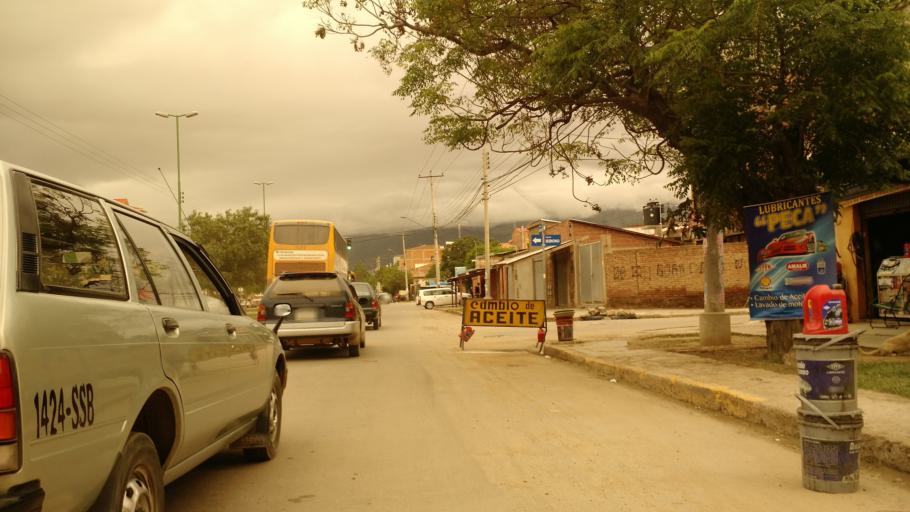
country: BO
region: Cochabamba
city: Cochabamba
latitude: -17.4184
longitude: -66.1660
